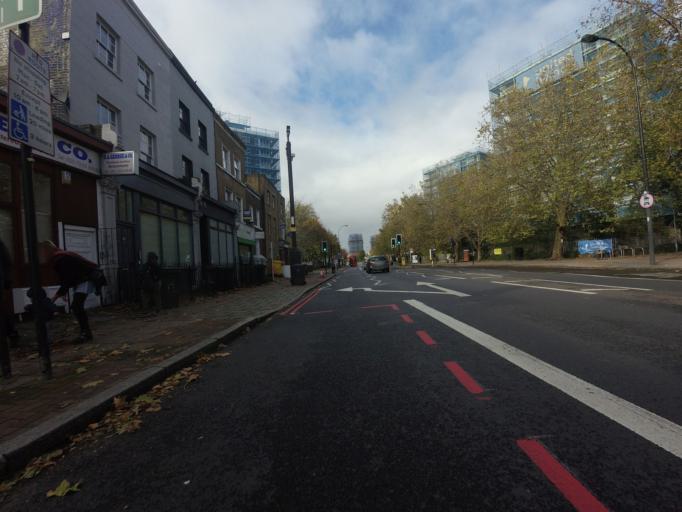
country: GB
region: England
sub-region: Greater London
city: Catford
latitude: 51.4764
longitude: -0.0488
